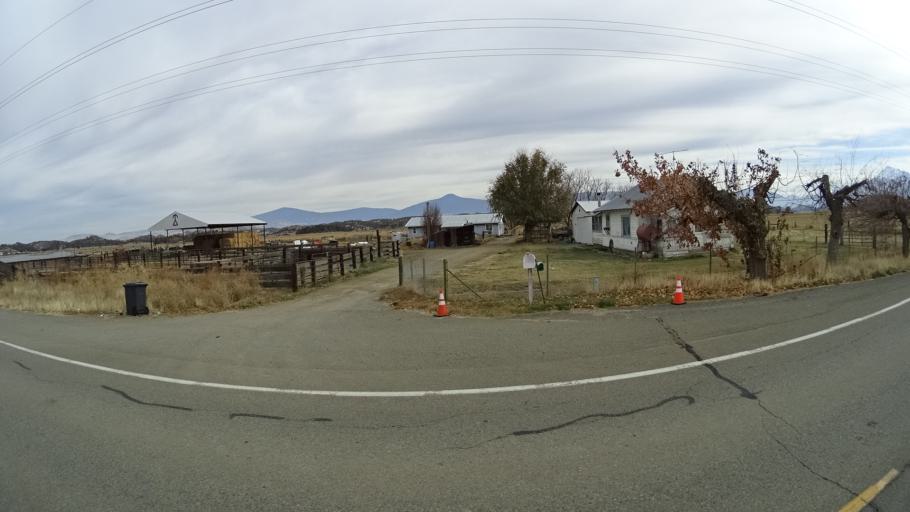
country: US
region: California
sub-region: Siskiyou County
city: Montague
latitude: 41.6618
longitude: -122.5211
